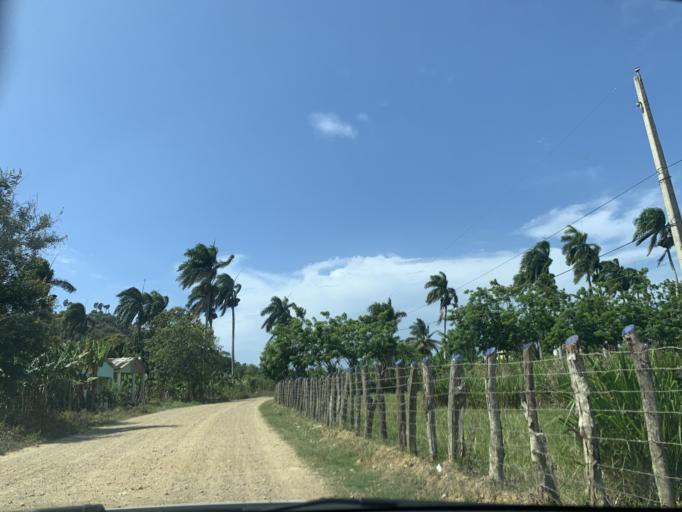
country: DO
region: Puerto Plata
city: Luperon
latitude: 19.8921
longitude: -70.8841
